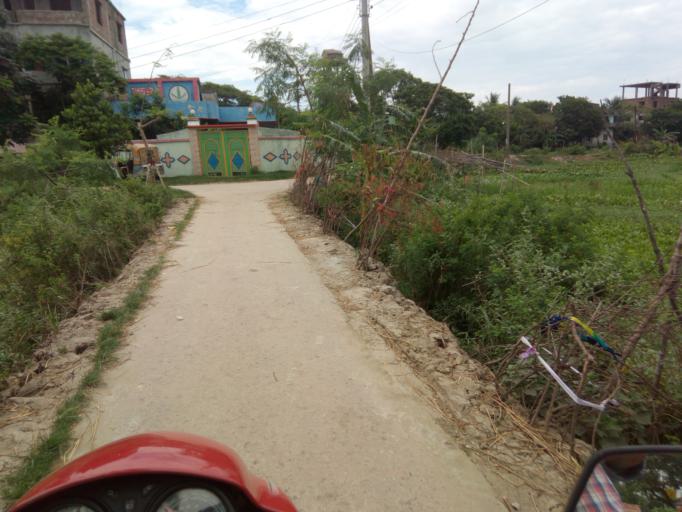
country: BD
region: Dhaka
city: Paltan
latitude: 23.7273
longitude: 90.4805
